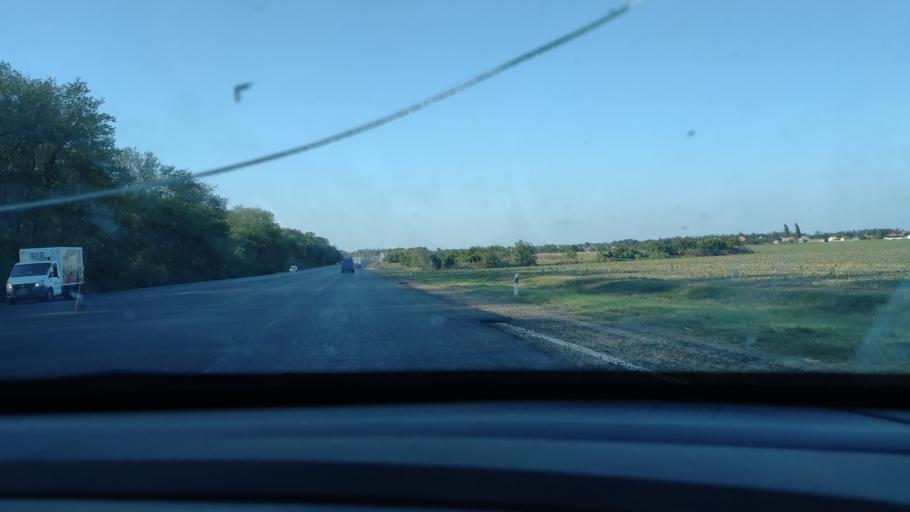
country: RU
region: Krasnodarskiy
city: Medvedovskaya
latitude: 45.5081
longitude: 38.9415
